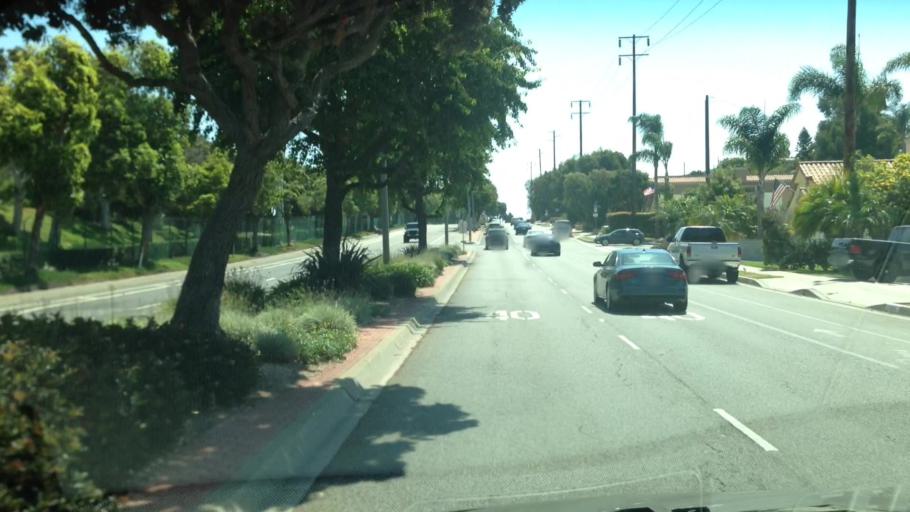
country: US
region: California
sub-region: Los Angeles County
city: Manhattan Beach
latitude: 33.9020
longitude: -118.4017
